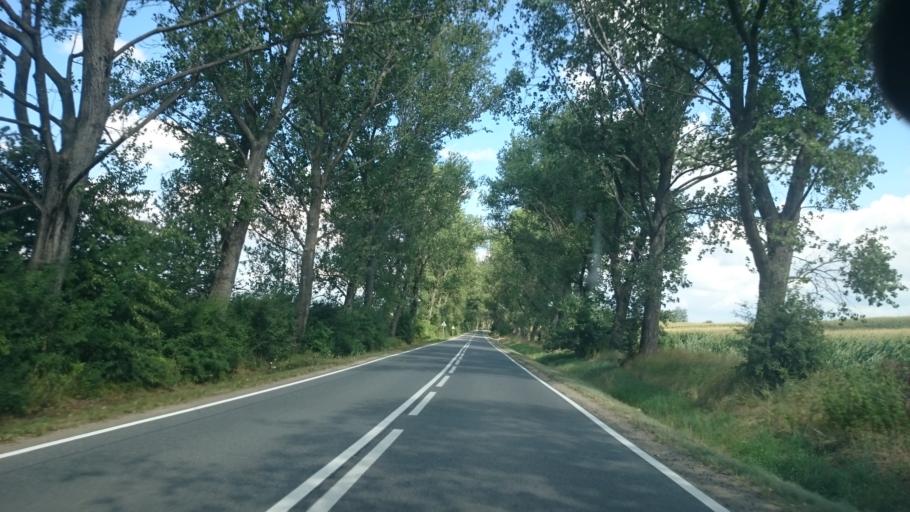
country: PL
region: Lower Silesian Voivodeship
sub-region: Powiat zabkowicki
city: Kamieniec Zabkowicki
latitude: 50.5429
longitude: 16.8637
